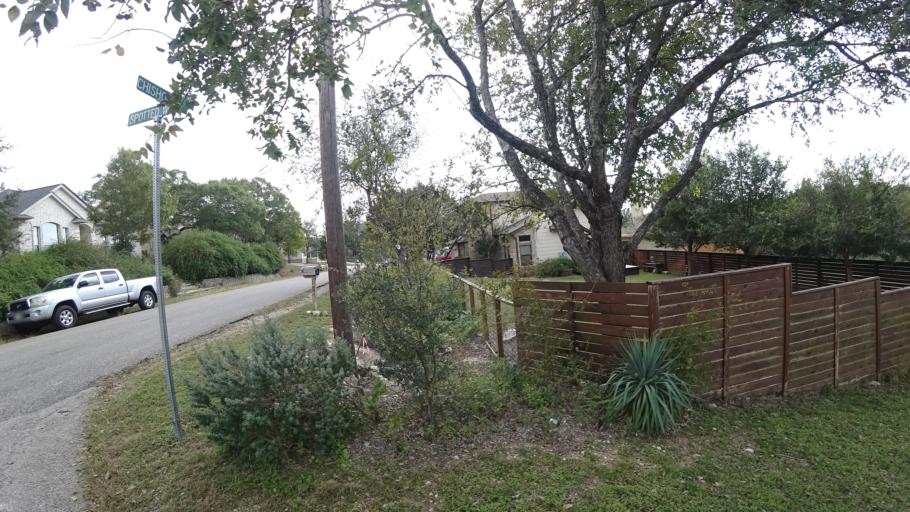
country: US
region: Texas
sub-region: Travis County
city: Hudson Bend
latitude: 30.3831
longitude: -97.9180
